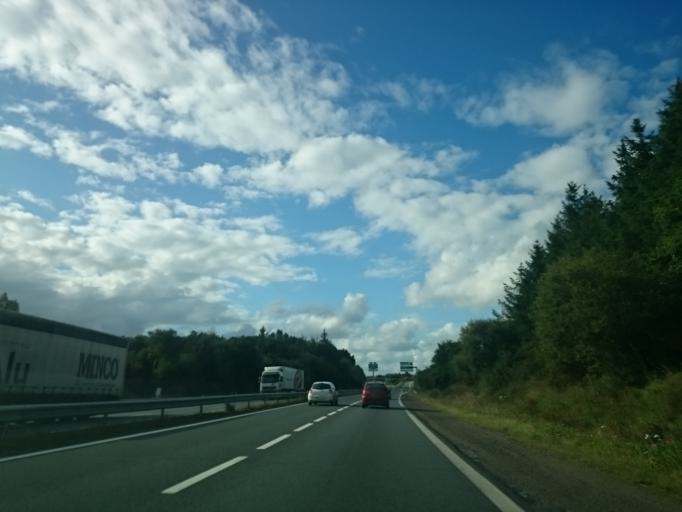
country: FR
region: Brittany
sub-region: Departement des Cotes-d'Armor
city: Plenee-Jugon
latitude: 48.4002
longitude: -2.4083
